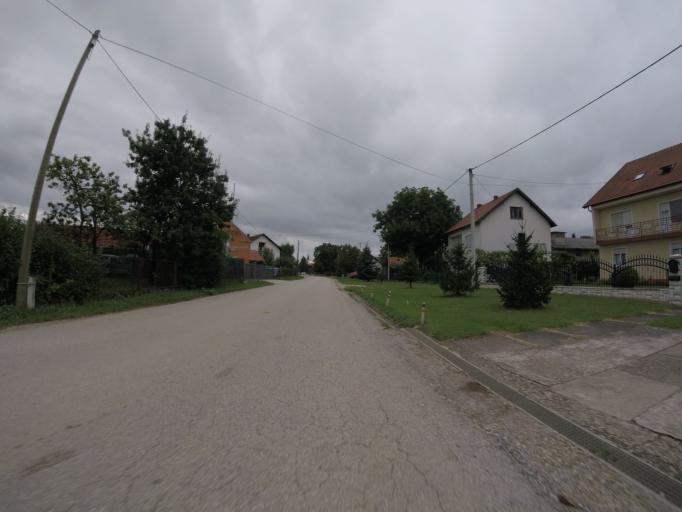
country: HR
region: Zagrebacka
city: Mraclin
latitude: 45.6640
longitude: 16.0981
